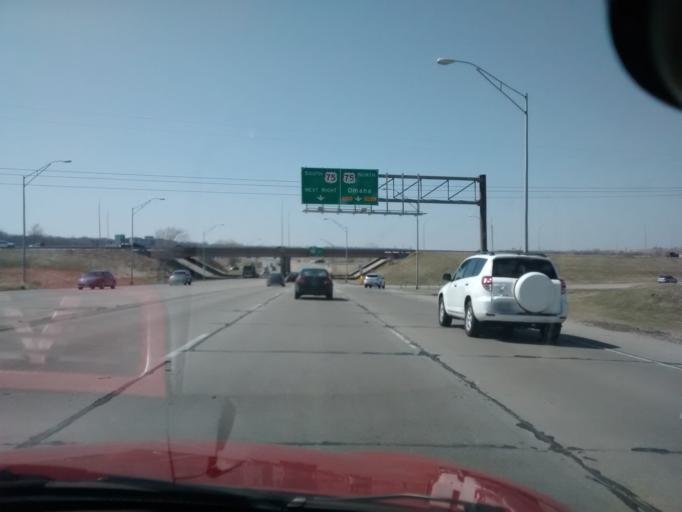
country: US
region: Nebraska
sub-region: Sarpy County
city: Offutt Air Force Base
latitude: 41.1402
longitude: -95.9349
